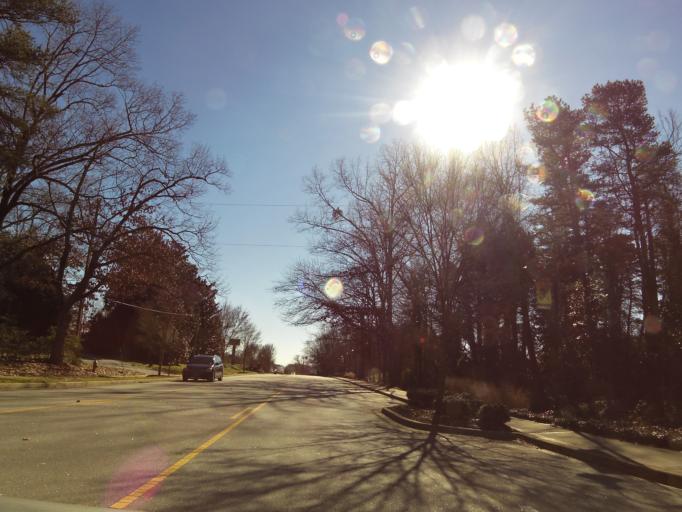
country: US
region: South Carolina
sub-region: Greenville County
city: Travelers Rest
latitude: 34.9598
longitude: -82.4402
